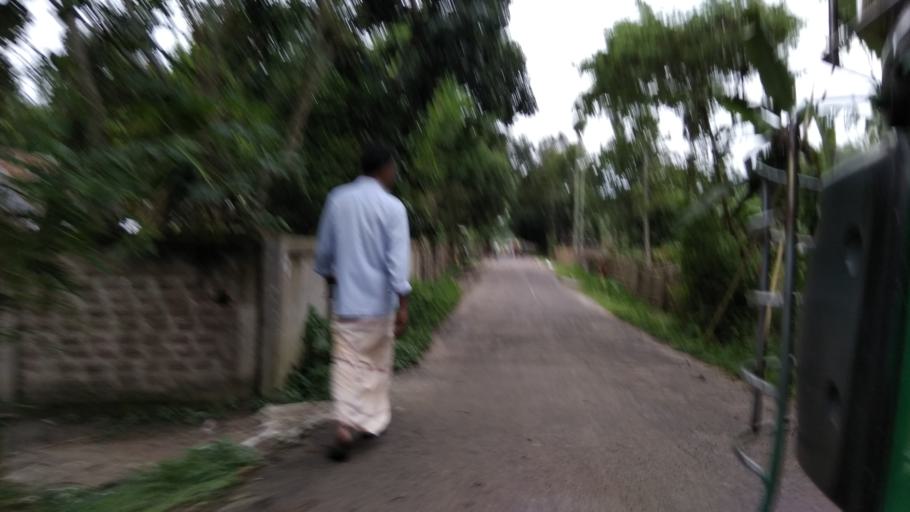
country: IN
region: Tripura
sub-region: Dhalai
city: Kamalpur
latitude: 24.2086
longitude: 91.8630
